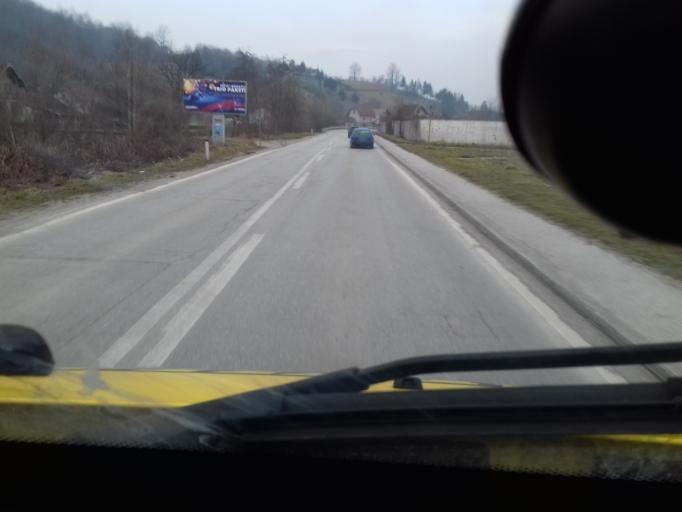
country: BA
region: Federation of Bosnia and Herzegovina
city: Busovaca
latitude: 44.1189
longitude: 17.8758
